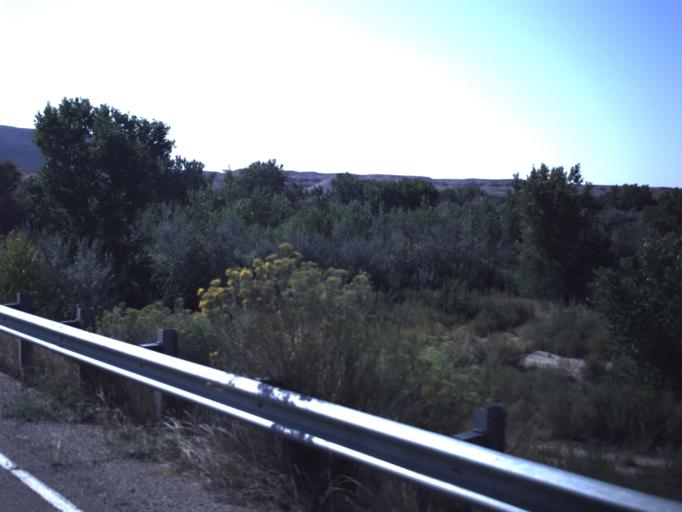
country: US
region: Utah
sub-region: San Juan County
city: Blanding
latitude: 37.2585
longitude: -109.6197
